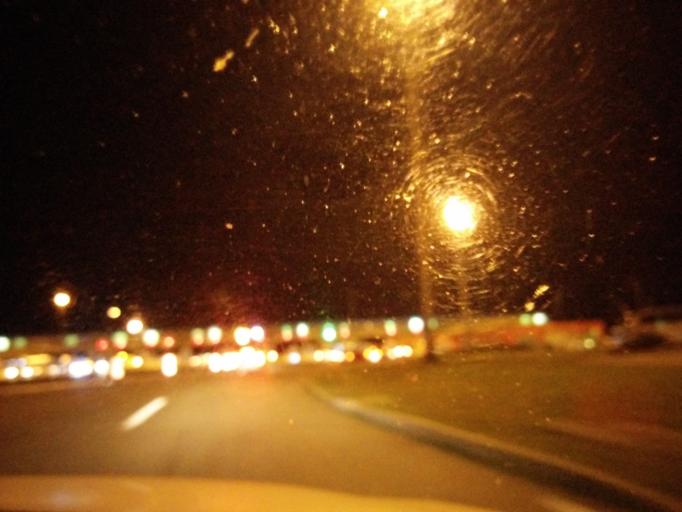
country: HR
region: Vukovarsko-Srijemska
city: Nijemci
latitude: 45.0481
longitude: 19.1005
